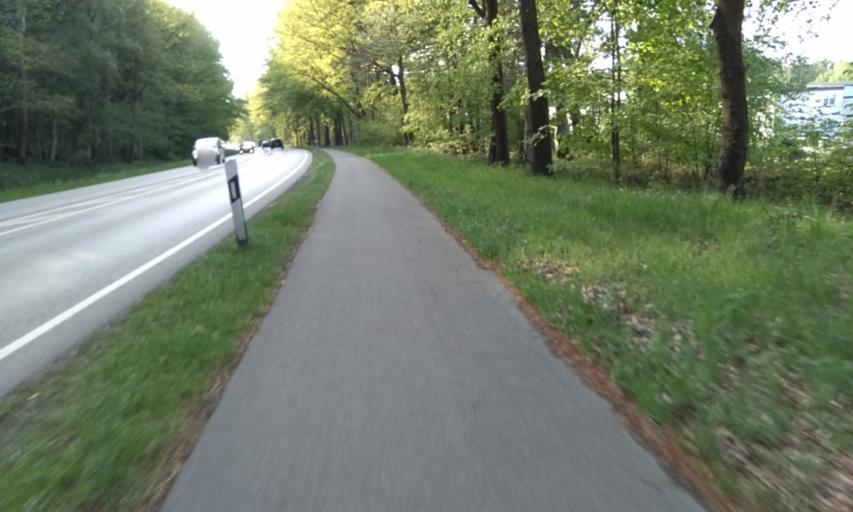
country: DE
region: Lower Saxony
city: Buxtehude
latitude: 53.4704
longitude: 9.6697
